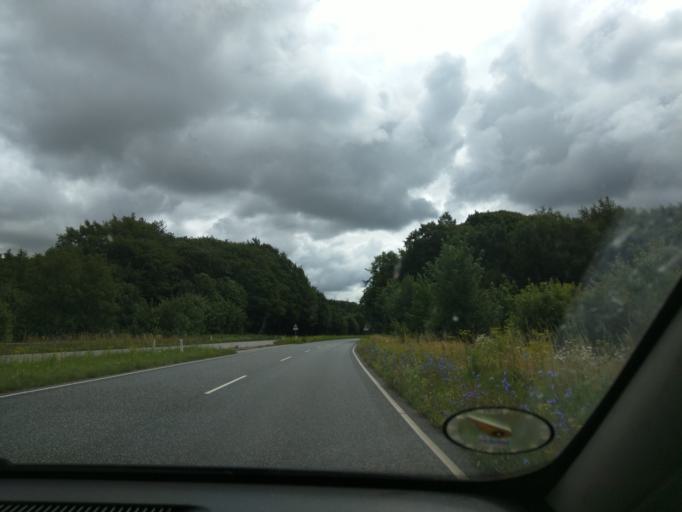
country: DK
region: Zealand
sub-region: Holbaek Kommune
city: Jyderup
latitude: 55.6695
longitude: 11.3609
